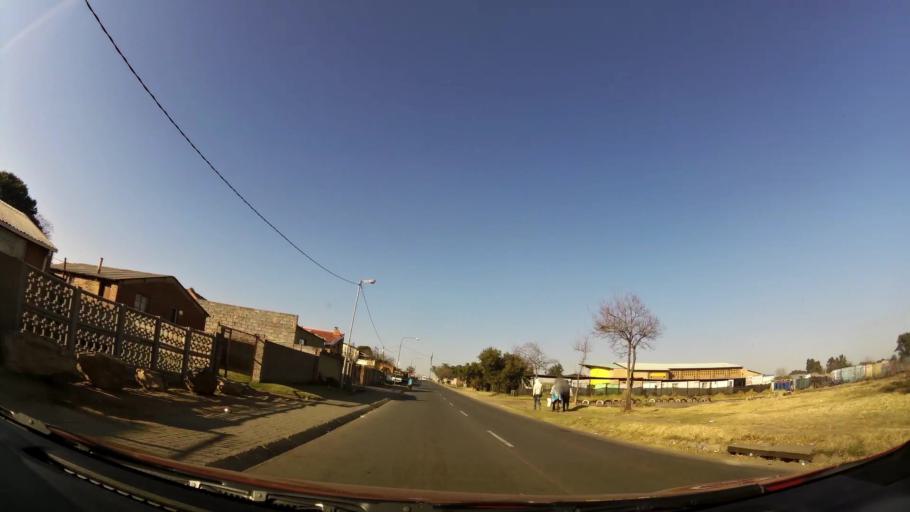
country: ZA
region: Gauteng
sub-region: City of Johannesburg Metropolitan Municipality
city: Soweto
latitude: -26.2412
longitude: 27.9408
